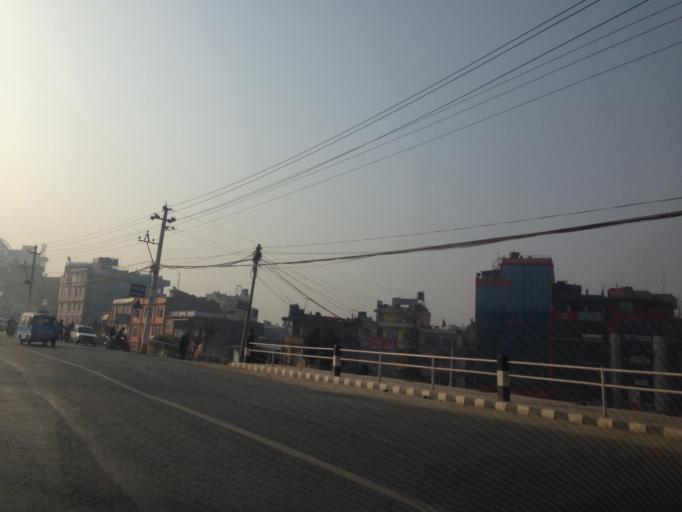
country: NP
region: Central Region
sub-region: Bagmati Zone
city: Kathmandu
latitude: 27.7029
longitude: 85.3522
